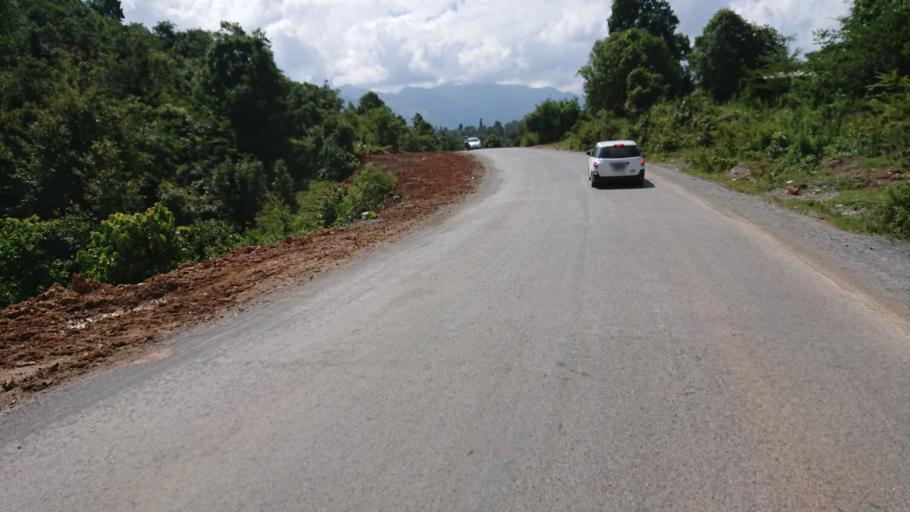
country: MM
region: Shan
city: Taunggyi
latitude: 20.8152
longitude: 97.3172
